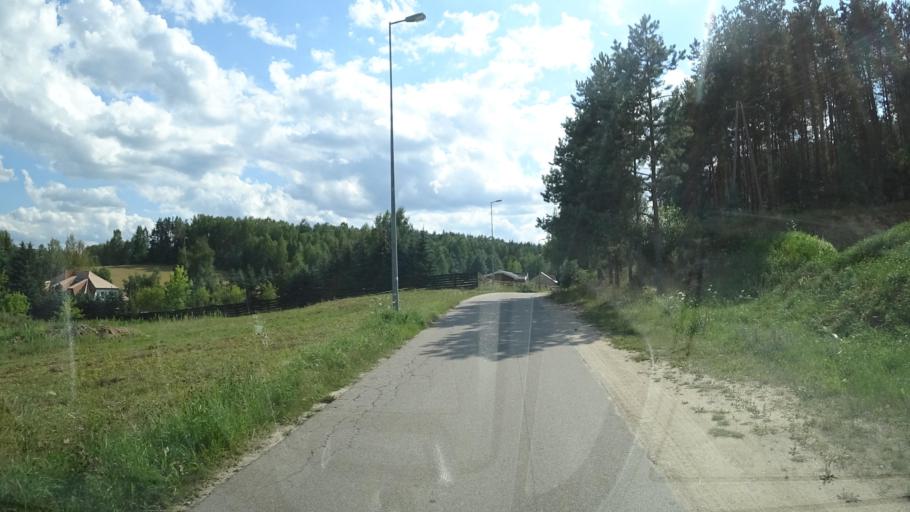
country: PL
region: Podlasie
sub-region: Powiat lomzynski
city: Piatnica
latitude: 53.1423
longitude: 22.1270
